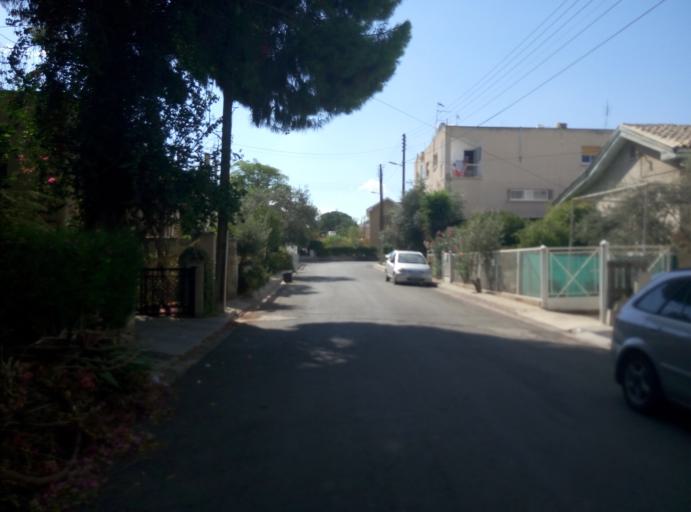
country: CY
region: Lefkosia
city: Nicosia
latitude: 35.1717
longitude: 33.3401
